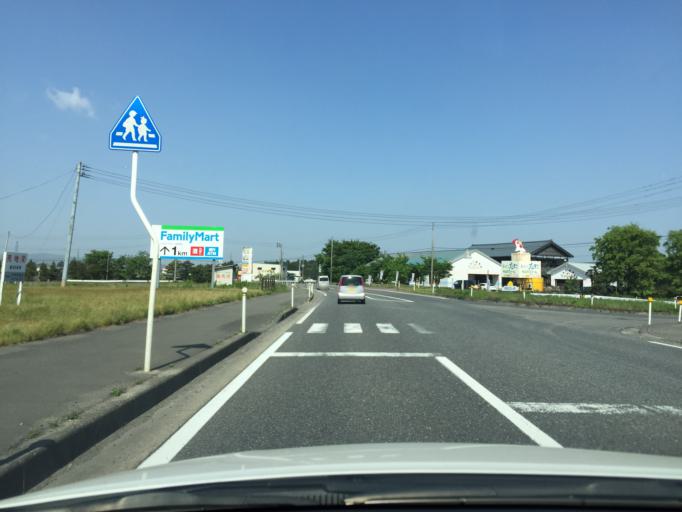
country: JP
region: Niigata
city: Gosen
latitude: 37.7484
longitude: 139.2122
